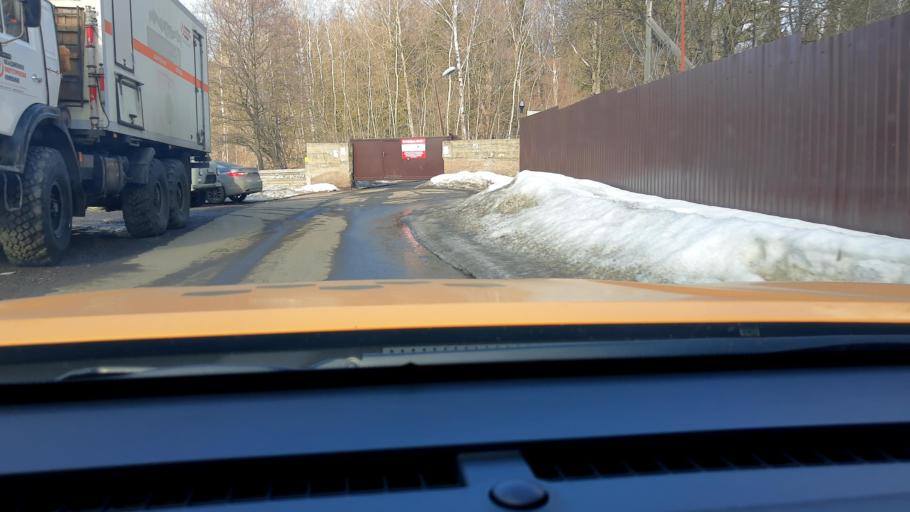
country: RU
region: Moskovskaya
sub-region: Leninskiy Rayon
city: Vnukovo
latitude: 55.6277
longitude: 37.2706
